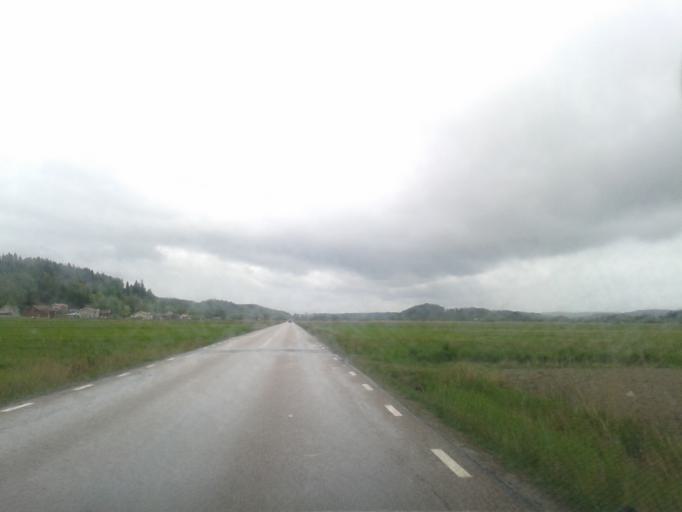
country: SE
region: Vaestra Goetaland
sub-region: Ale Kommun
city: Alvangen
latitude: 57.9826
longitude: 12.1133
